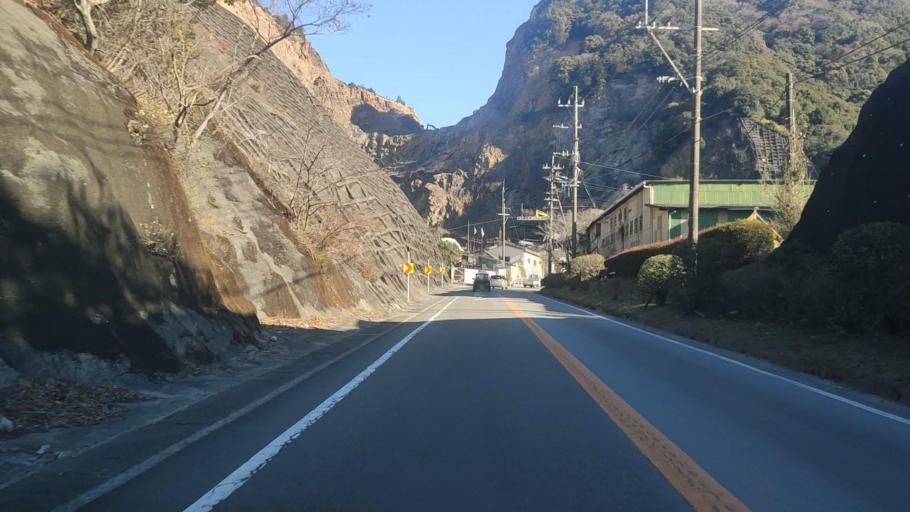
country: JP
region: Miyazaki
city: Nobeoka
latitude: 32.6279
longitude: 131.7169
